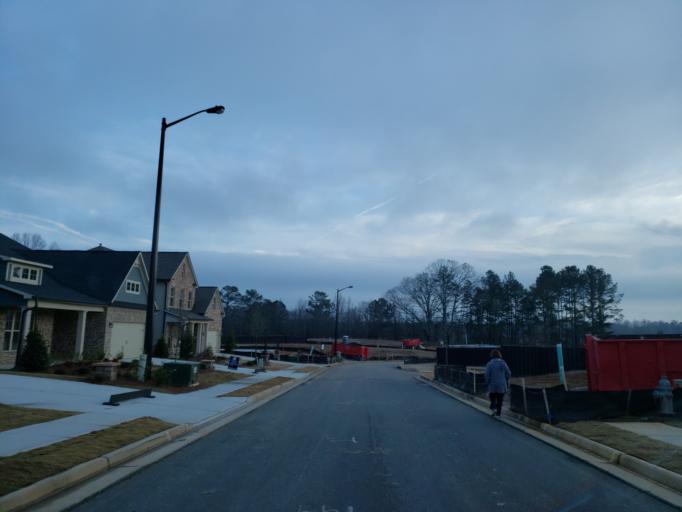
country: US
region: Georgia
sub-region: Cherokee County
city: Ball Ground
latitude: 34.2451
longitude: -84.3531
